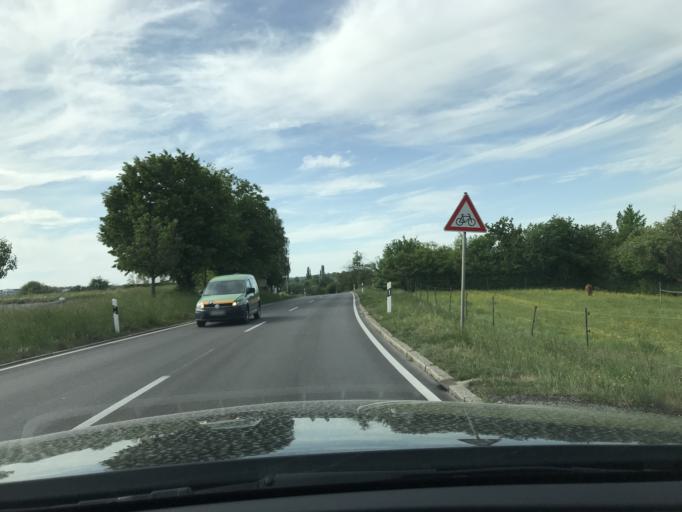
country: DE
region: Baden-Wuerttemberg
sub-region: Regierungsbezirk Stuttgart
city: Waiblingen
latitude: 48.8187
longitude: 9.3370
